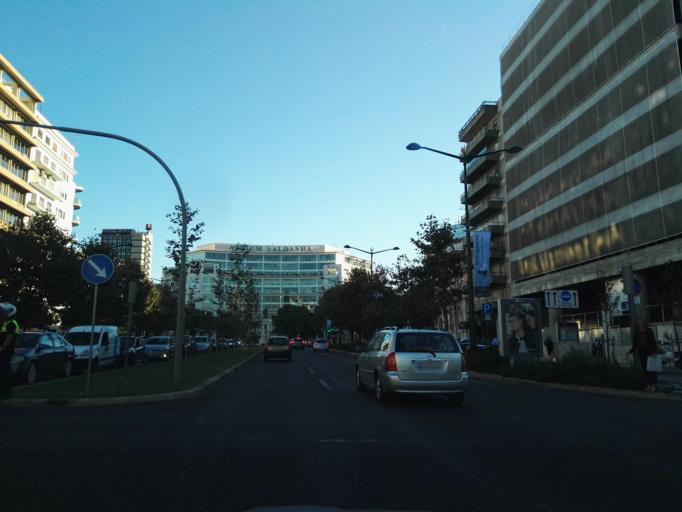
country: PT
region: Lisbon
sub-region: Lisbon
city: Lisbon
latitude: 38.7352
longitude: -9.1453
